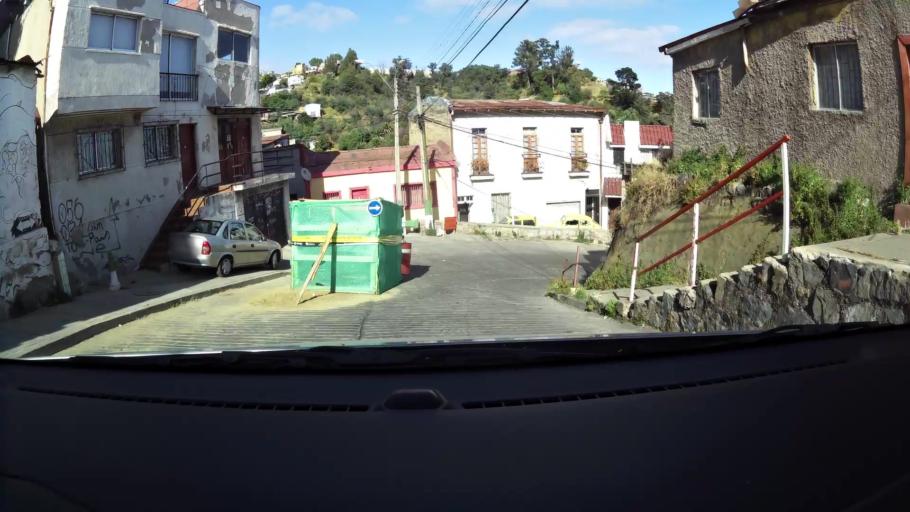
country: CL
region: Valparaiso
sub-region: Provincia de Valparaiso
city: Valparaiso
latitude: -33.0546
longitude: -71.6010
